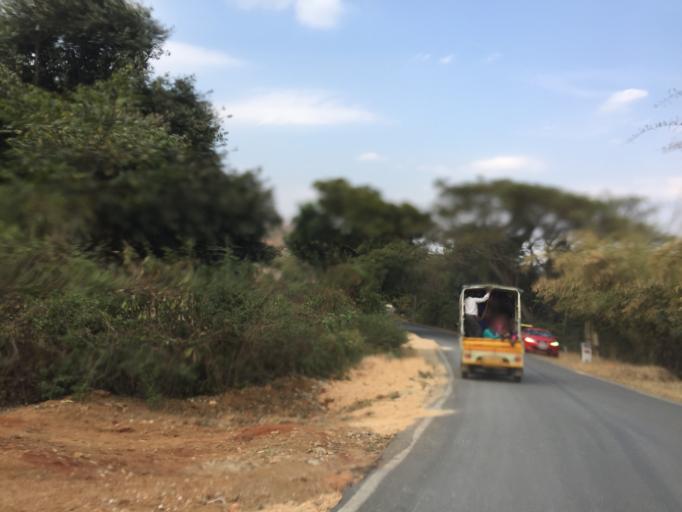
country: IN
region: Karnataka
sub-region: Chikkaballapur
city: Chik Ballapur
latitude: 13.3785
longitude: 77.6741
